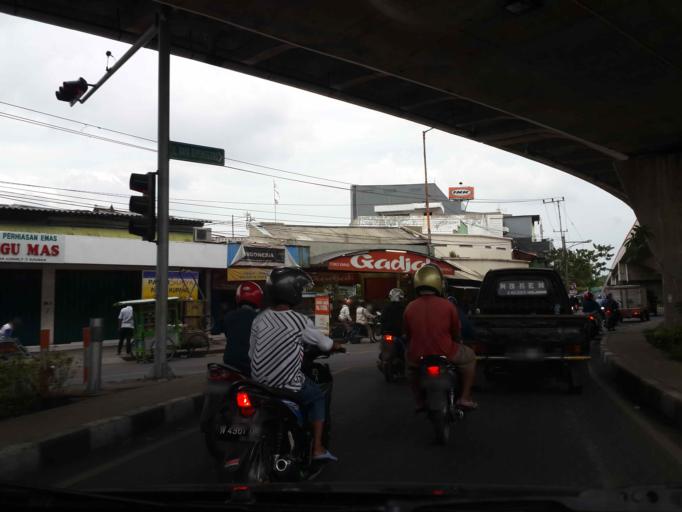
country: ID
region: East Java
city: Gubengairlangga
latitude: -7.2750
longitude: 112.7267
